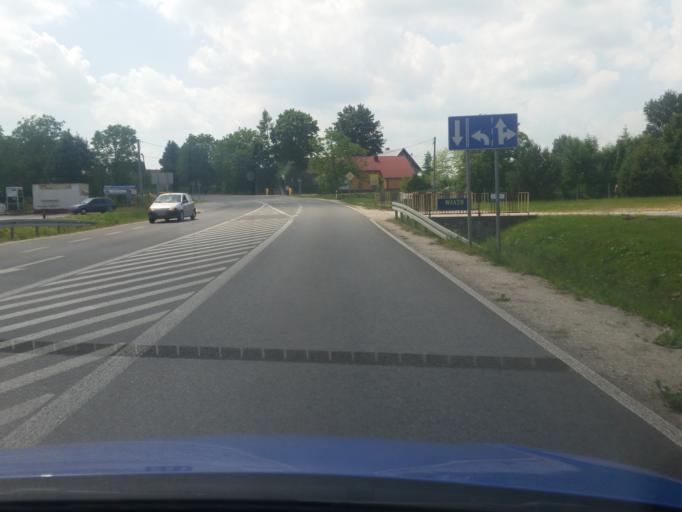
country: PL
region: Swietokrzyskie
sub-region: Powiat kazimierski
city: Czarnocin
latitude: 50.3211
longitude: 20.5422
